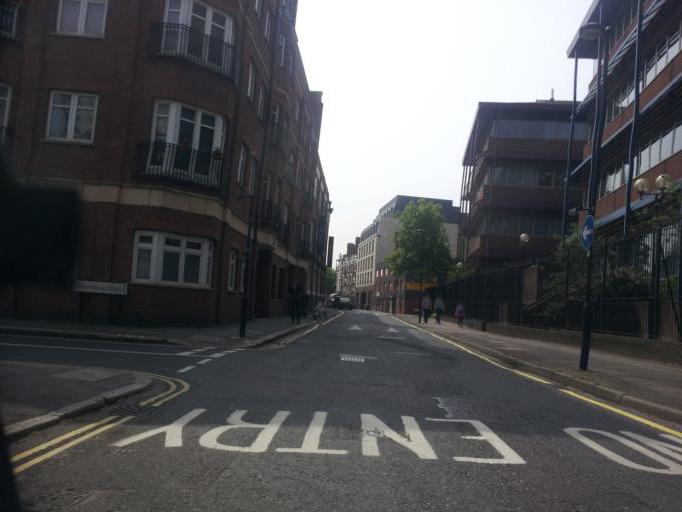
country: GB
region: England
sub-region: Greater London
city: City of Westminster
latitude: 51.4901
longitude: -0.1199
